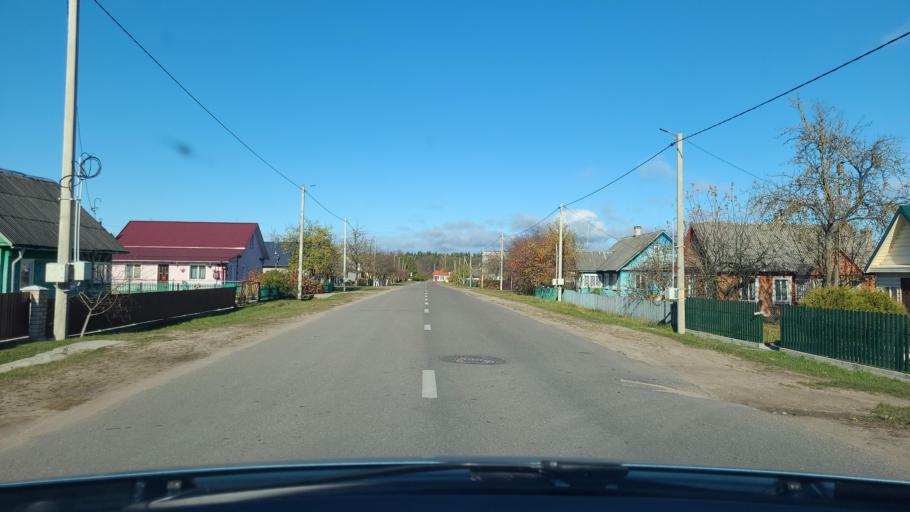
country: BY
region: Grodnenskaya
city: Astravyets
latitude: 54.6155
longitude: 25.9457
